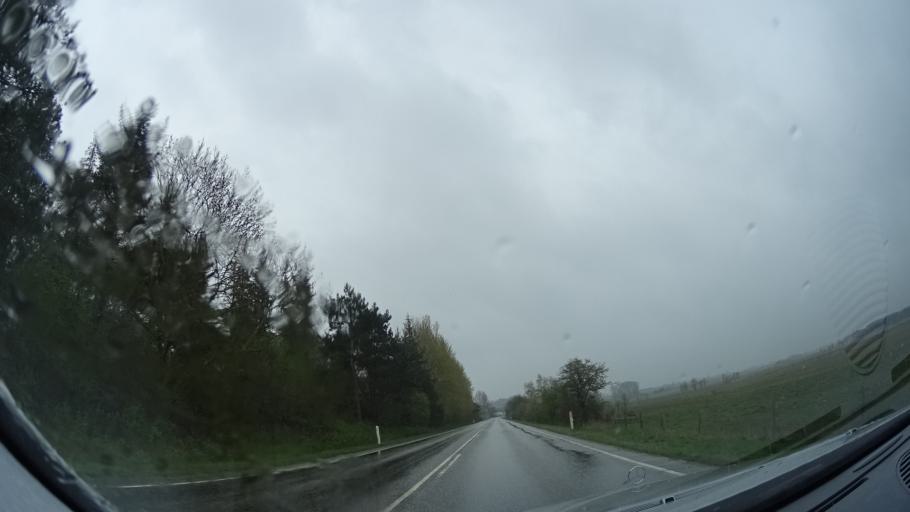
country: DK
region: Zealand
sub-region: Holbaek Kommune
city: Holbaek
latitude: 55.7642
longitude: 11.6303
